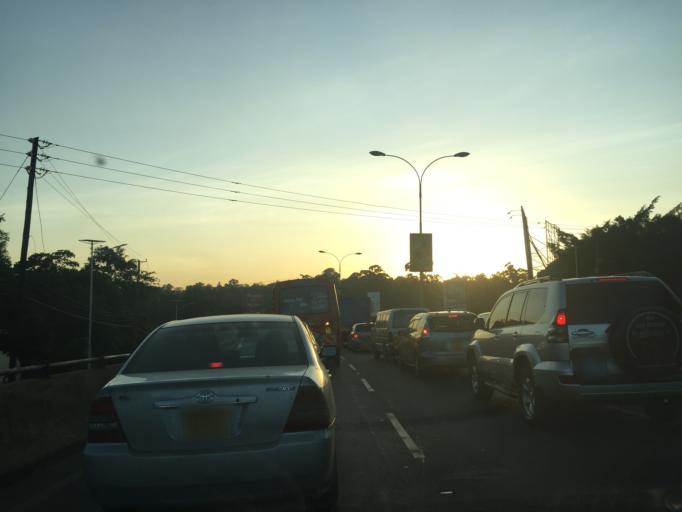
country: KE
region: Nairobi Area
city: Nairobi
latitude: -1.2735
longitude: 36.8135
